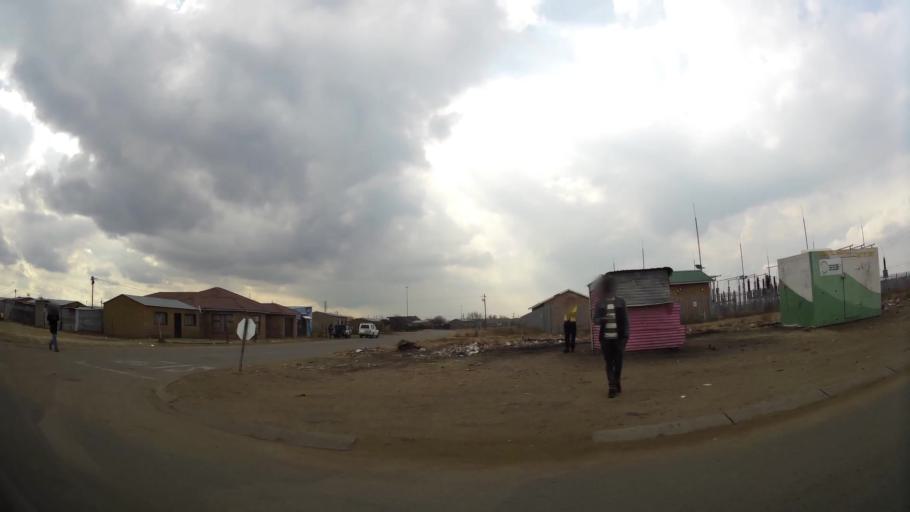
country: ZA
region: Orange Free State
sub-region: Fezile Dabi District Municipality
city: Sasolburg
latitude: -26.8560
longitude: 27.8862
